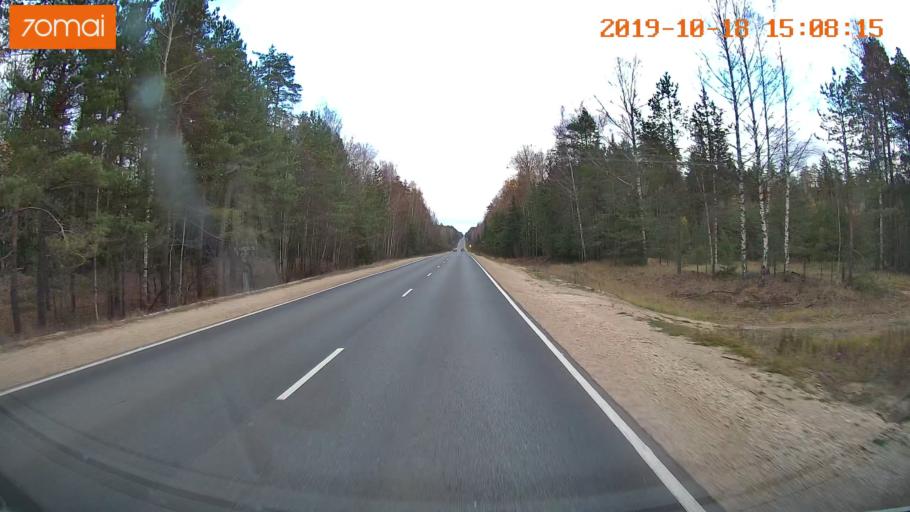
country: RU
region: Vladimir
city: Gus'-Khrustal'nyy
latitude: 55.5497
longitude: 40.6085
